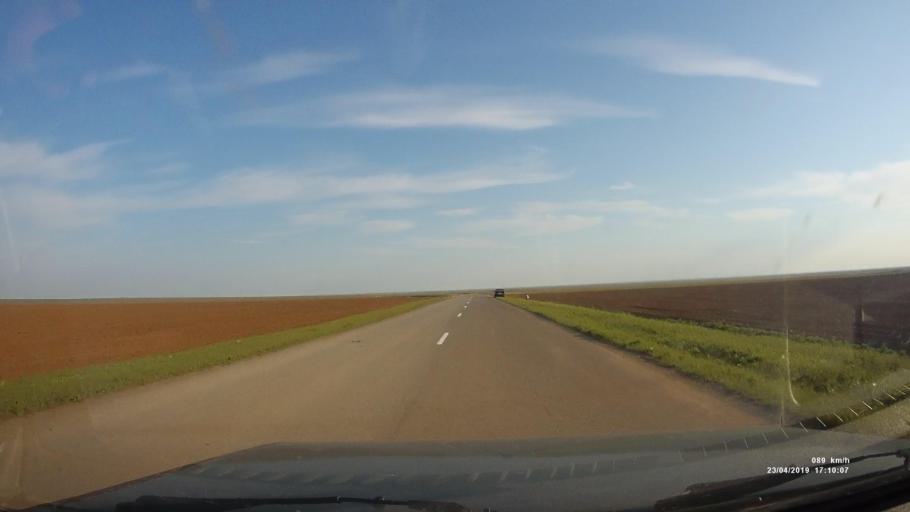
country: RU
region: Kalmykiya
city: Priyutnoye
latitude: 46.2490
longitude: 43.4841
